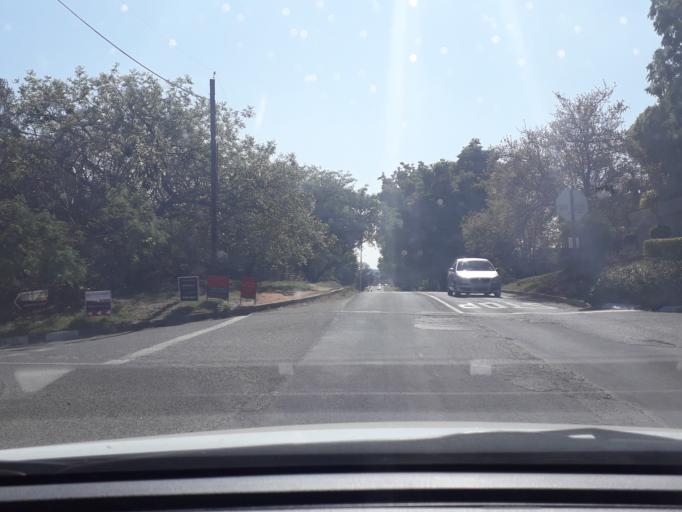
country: ZA
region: Gauteng
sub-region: City of Johannesburg Metropolitan Municipality
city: Roodepoort
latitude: -26.0829
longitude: 27.9588
